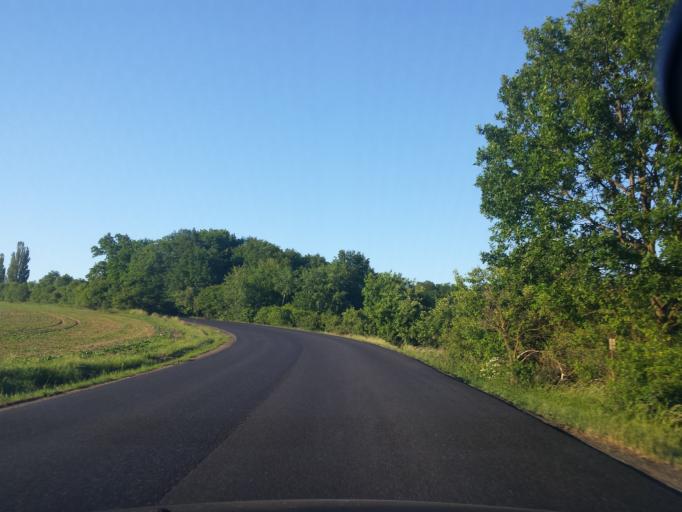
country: CZ
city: Duba
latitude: 50.5666
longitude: 14.5436
